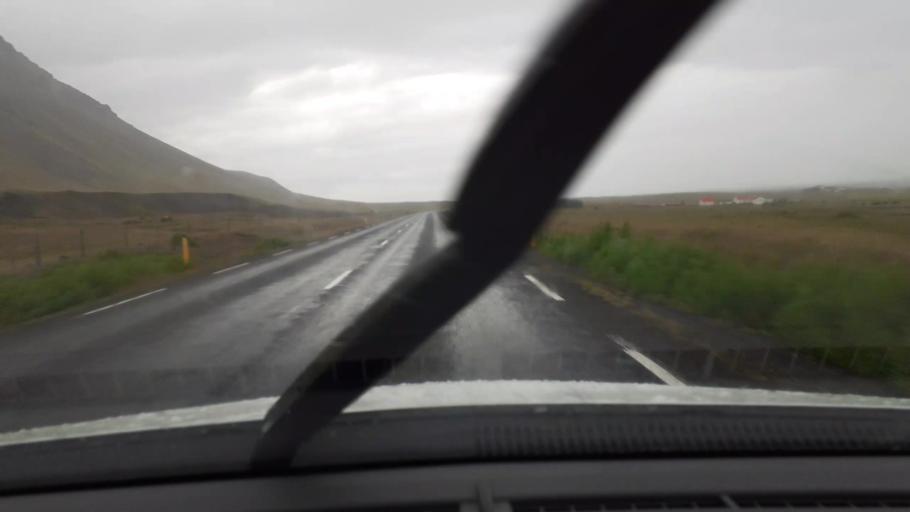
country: IS
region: West
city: Borgarnes
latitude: 64.3663
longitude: -21.8926
